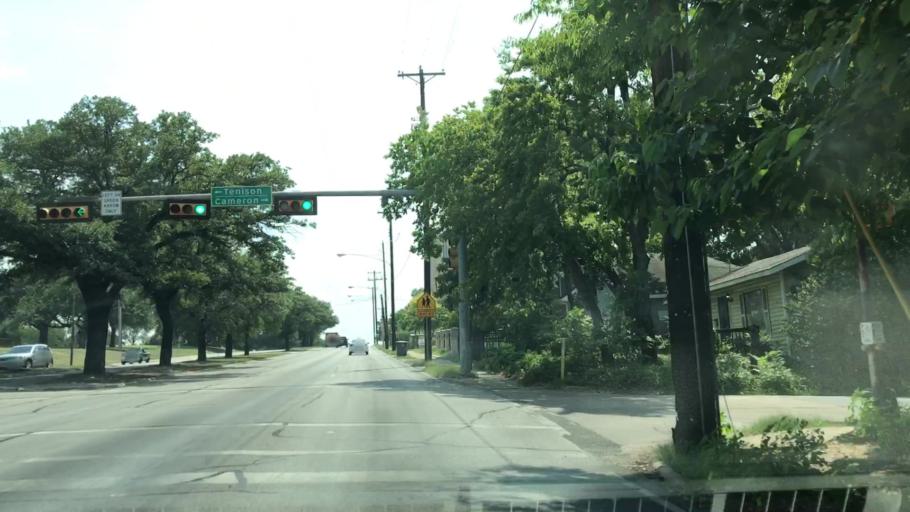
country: US
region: Texas
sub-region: Dallas County
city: Highland Park
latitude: 32.7994
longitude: -96.7412
